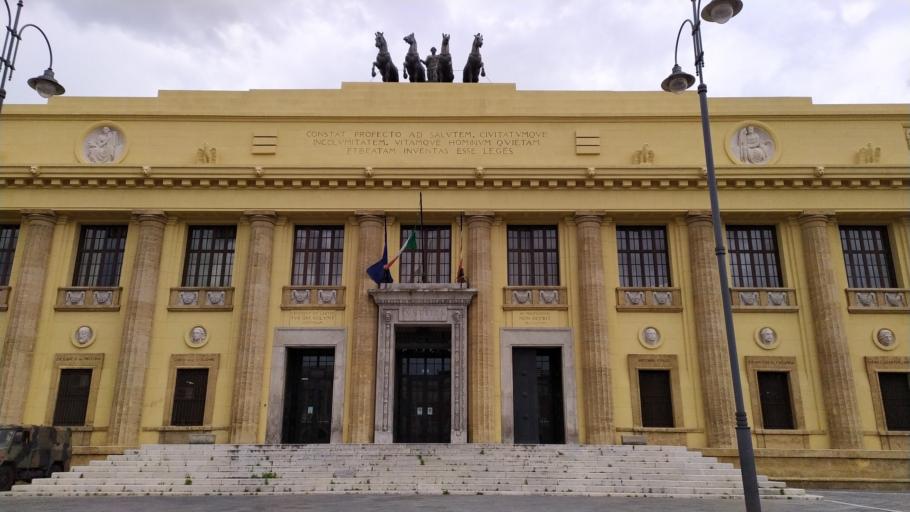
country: IT
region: Sicily
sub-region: Messina
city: Messina
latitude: 38.1887
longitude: 15.5526
